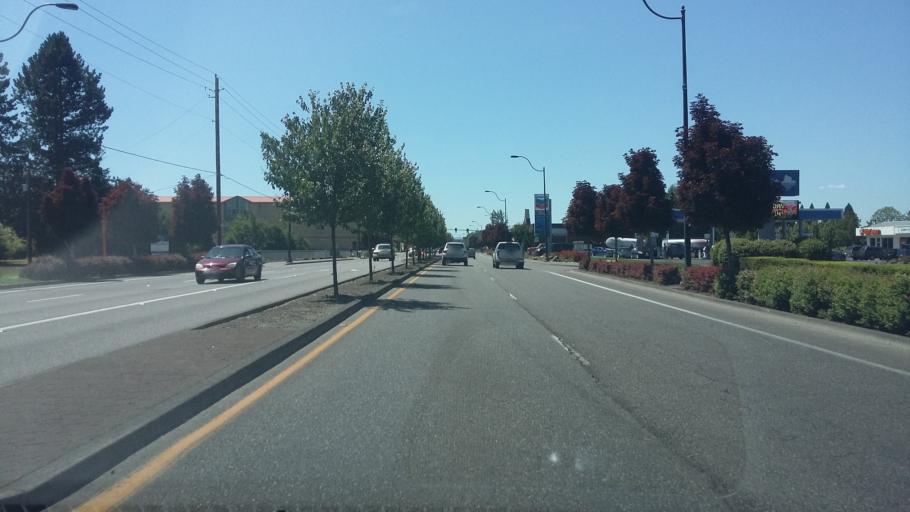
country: US
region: Washington
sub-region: Clark County
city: Battle Ground
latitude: 45.7808
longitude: -122.5501
